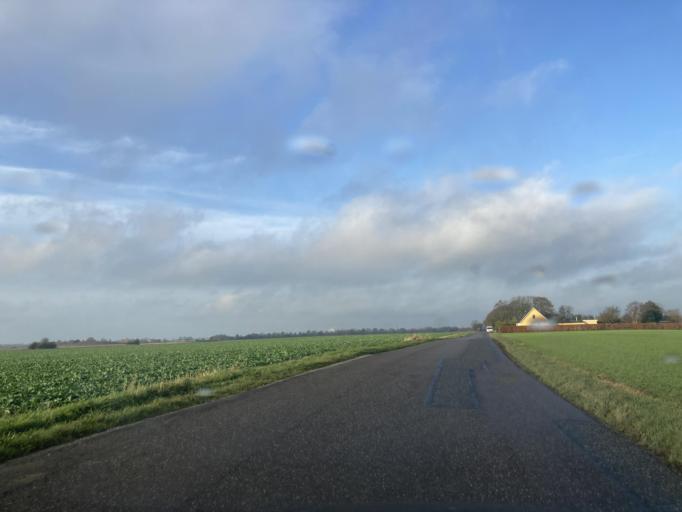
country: DK
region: Zealand
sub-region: Lolland Kommune
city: Rodby
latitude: 54.6819
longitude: 11.4103
